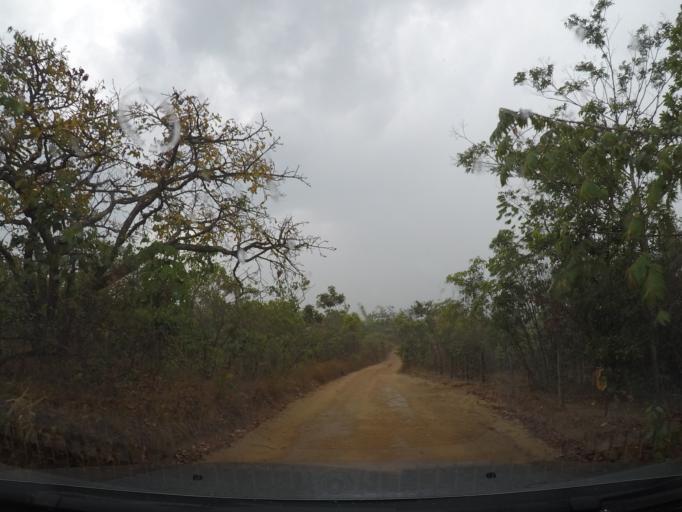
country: BR
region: Goias
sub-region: Pirenopolis
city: Pirenopolis
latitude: -15.8349
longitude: -48.8850
